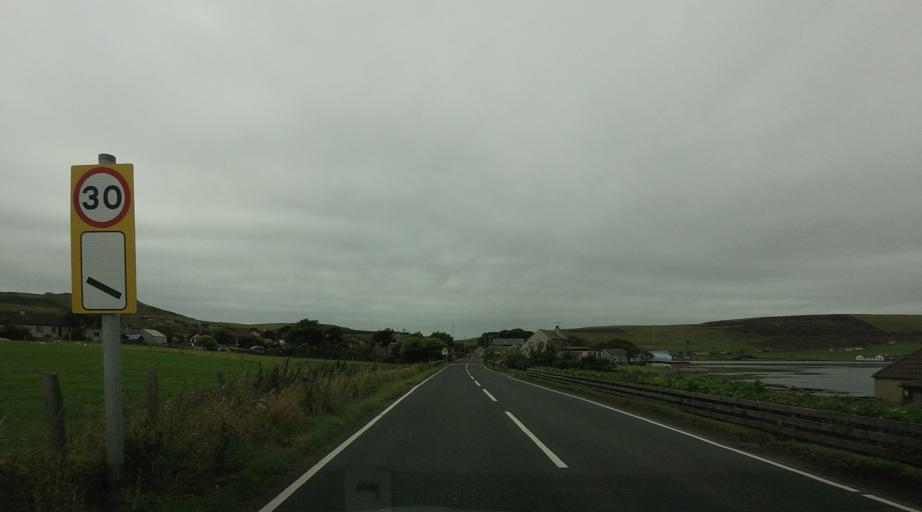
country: GB
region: Scotland
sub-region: Orkney Islands
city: Orkney
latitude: 59.0022
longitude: -3.1041
